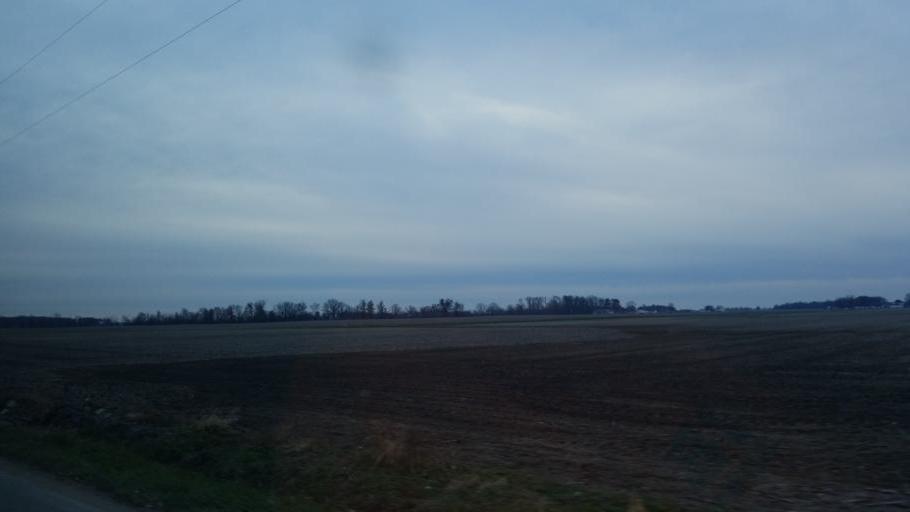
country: US
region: Indiana
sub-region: Adams County
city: Decatur
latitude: 40.7763
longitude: -84.8799
